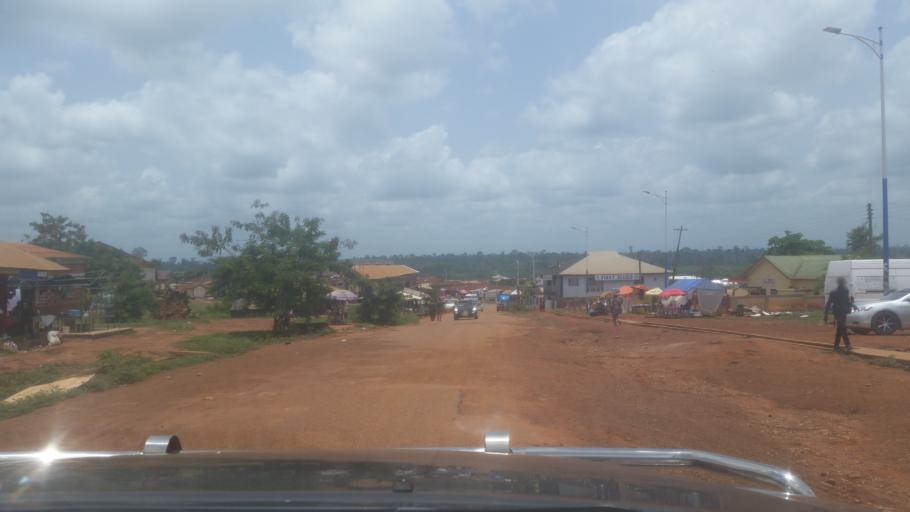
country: GH
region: Western
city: Bibiani
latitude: 6.8036
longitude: -2.5191
